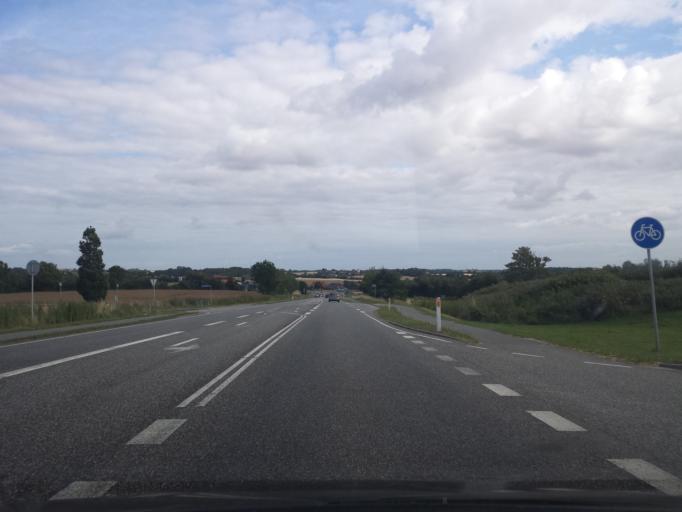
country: DK
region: South Denmark
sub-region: Sonderborg Kommune
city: Guderup
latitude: 54.9808
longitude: 9.8783
